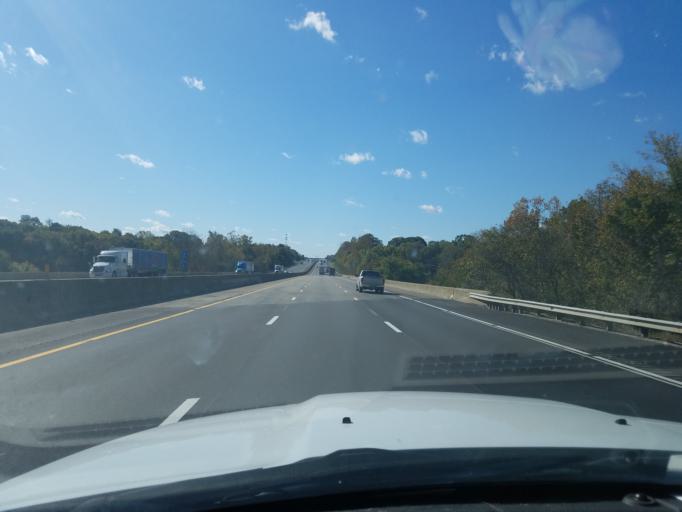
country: US
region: Kentucky
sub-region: Warren County
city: Bowling Green
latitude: 36.9897
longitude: -86.3847
